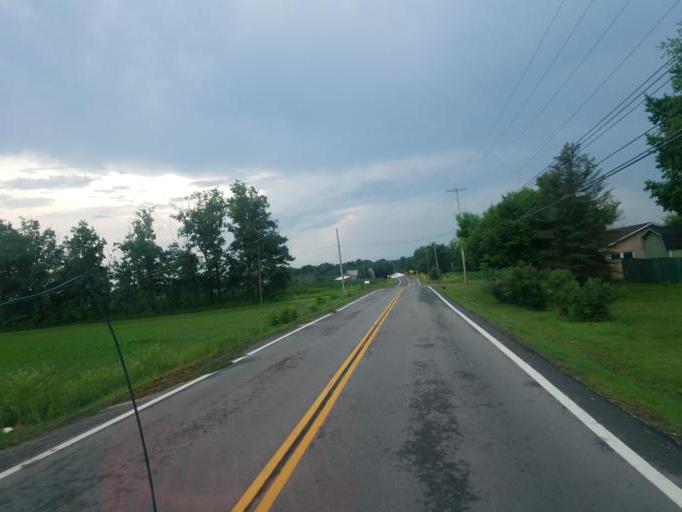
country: US
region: Ohio
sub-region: Wayne County
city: Doylestown
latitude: 40.9610
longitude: -81.7385
